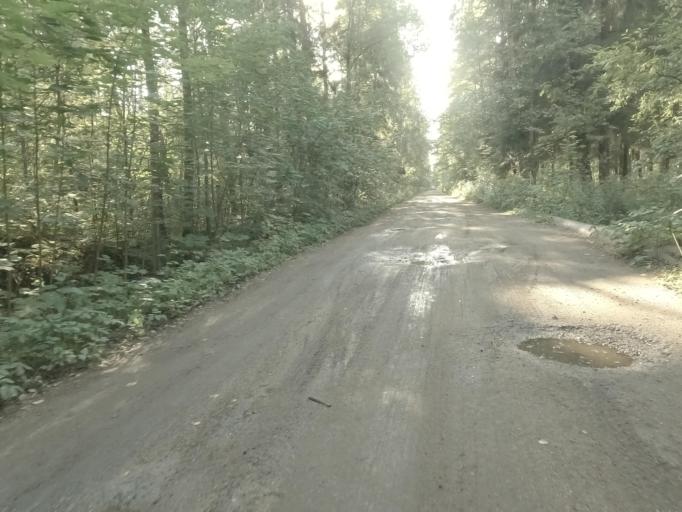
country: RU
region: Leningrad
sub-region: Volosovskiy Rayon
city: Shlissel'burg
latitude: 59.9461
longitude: 30.9991
